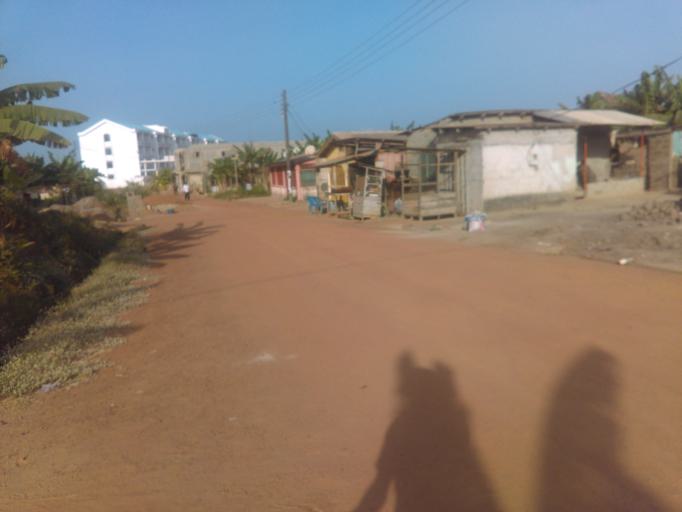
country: GH
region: Central
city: Cape Coast
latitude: 5.1092
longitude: -1.2985
